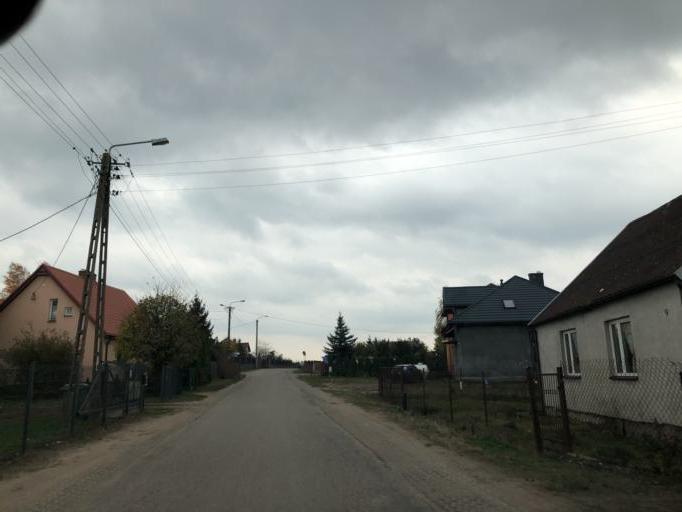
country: PL
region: Podlasie
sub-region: Lomza
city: Lomza
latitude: 53.1651
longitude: 21.9987
